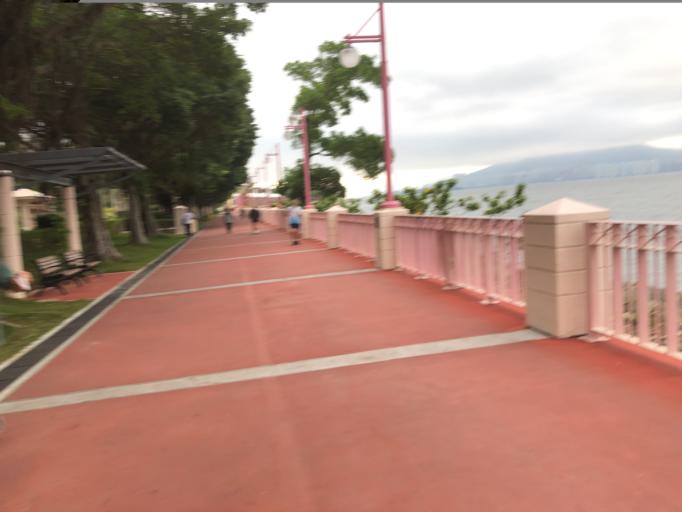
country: HK
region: Tai Po
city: Tai Po
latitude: 22.4527
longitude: 114.1845
